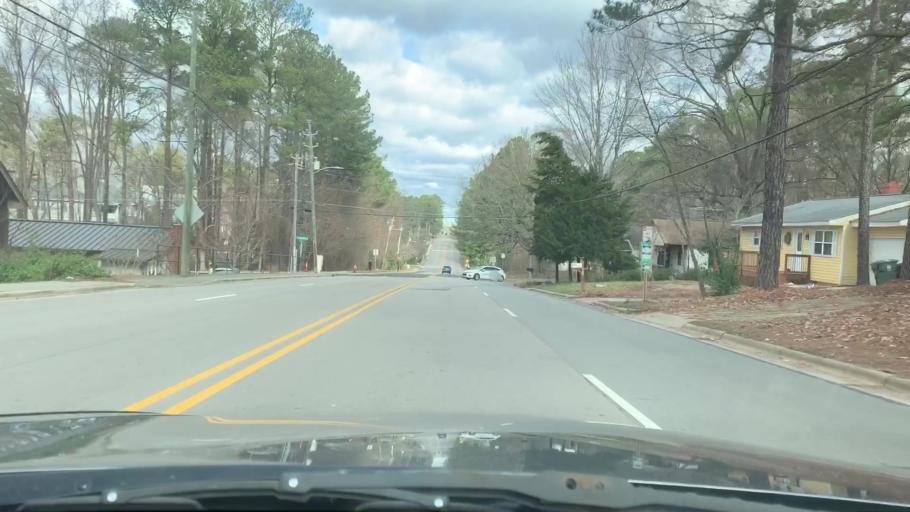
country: US
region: North Carolina
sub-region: Wake County
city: Cary
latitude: 35.7938
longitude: -78.7831
